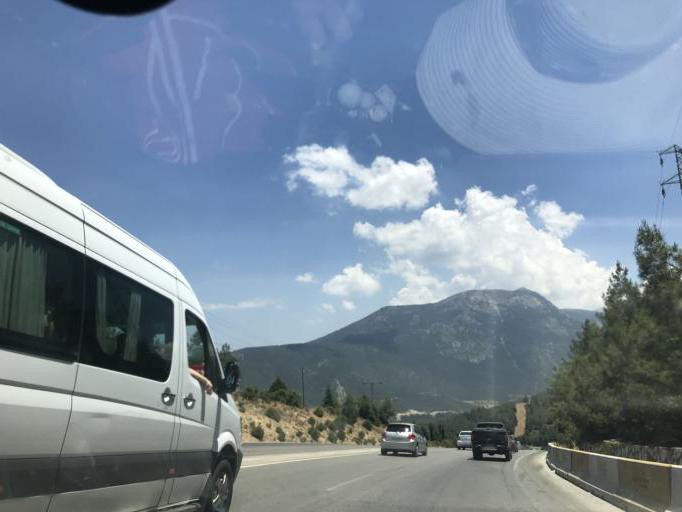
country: TR
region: Denizli
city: Honaz
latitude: 37.7326
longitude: 29.1802
